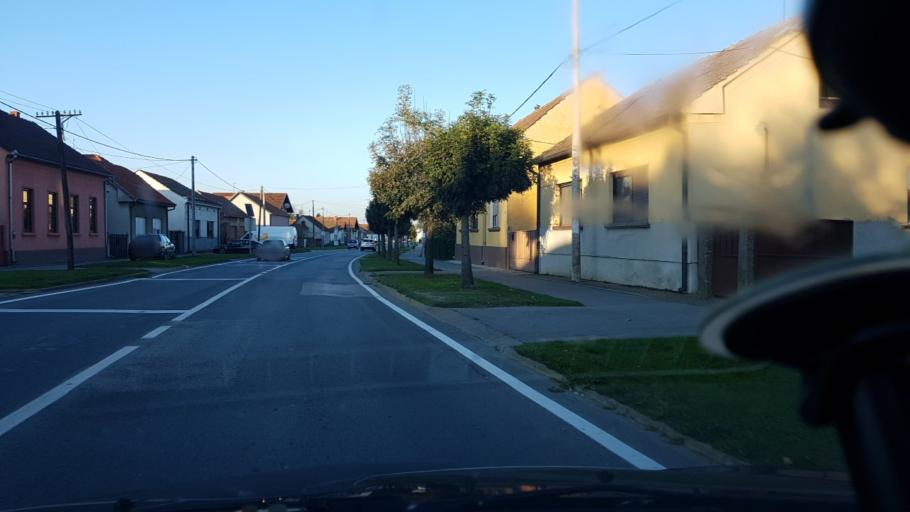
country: HR
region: Koprivnicko-Krizevacka
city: Virje
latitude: 46.0776
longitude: 16.9505
